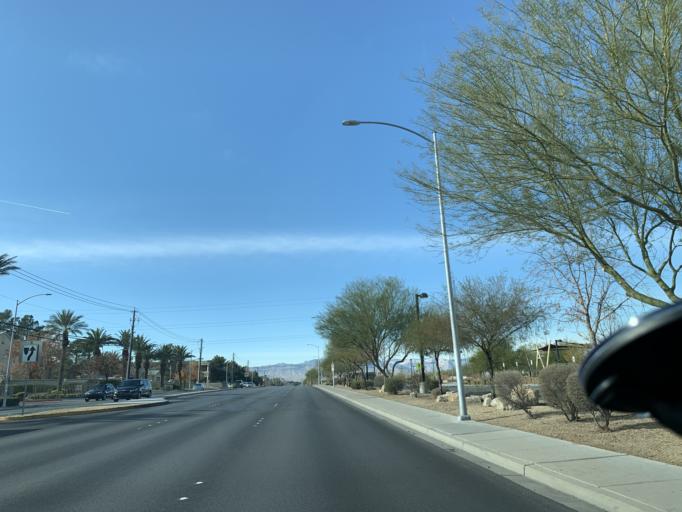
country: US
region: Nevada
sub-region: Clark County
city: Spring Valley
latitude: 36.1008
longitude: -115.2104
